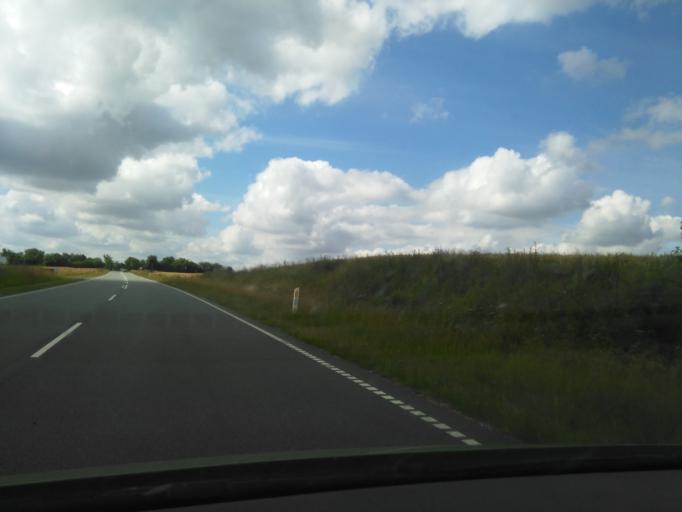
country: DK
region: Central Jutland
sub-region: Arhus Kommune
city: Solbjerg
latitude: 56.0231
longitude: 10.0490
